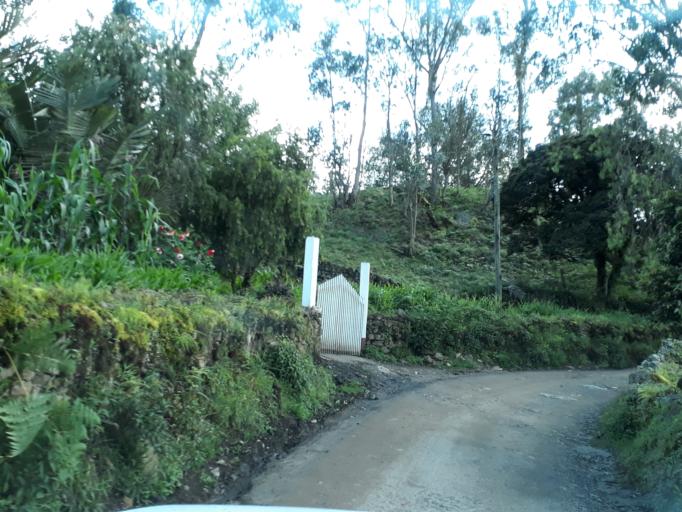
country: CO
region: Cundinamarca
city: Junin
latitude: 4.7914
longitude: -73.6688
